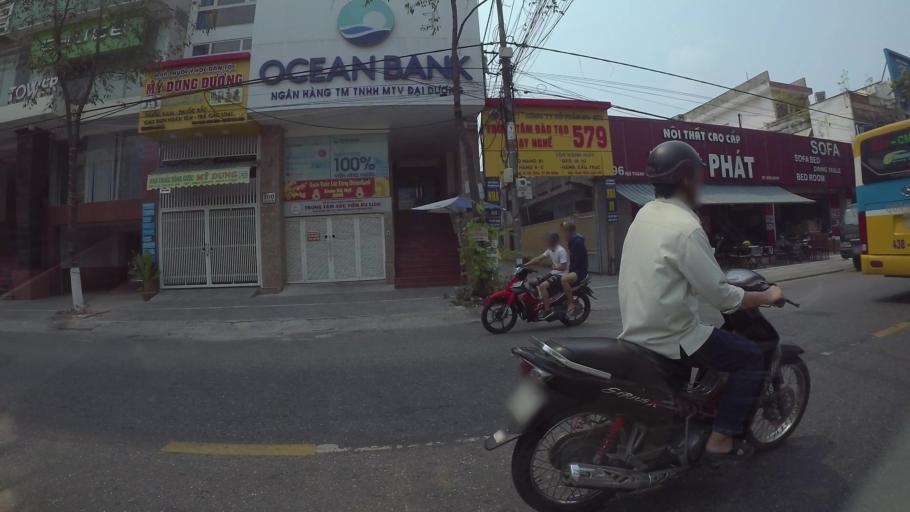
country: VN
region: Da Nang
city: Son Tra
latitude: 16.0513
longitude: 108.2205
